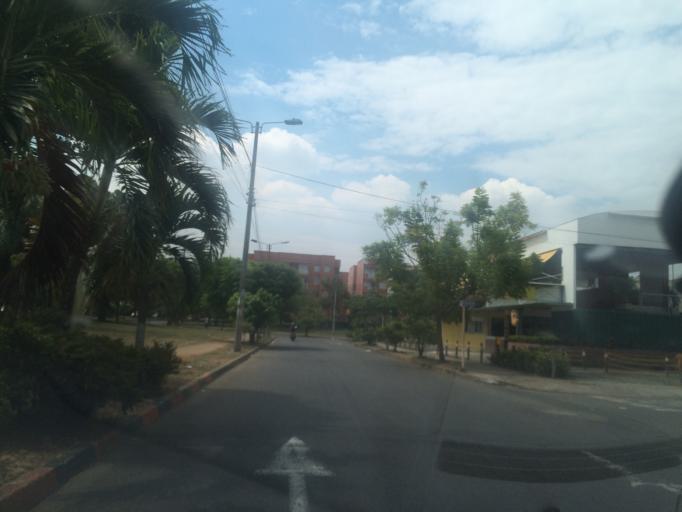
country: CO
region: Valle del Cauca
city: Cali
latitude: 3.3768
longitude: -76.5201
